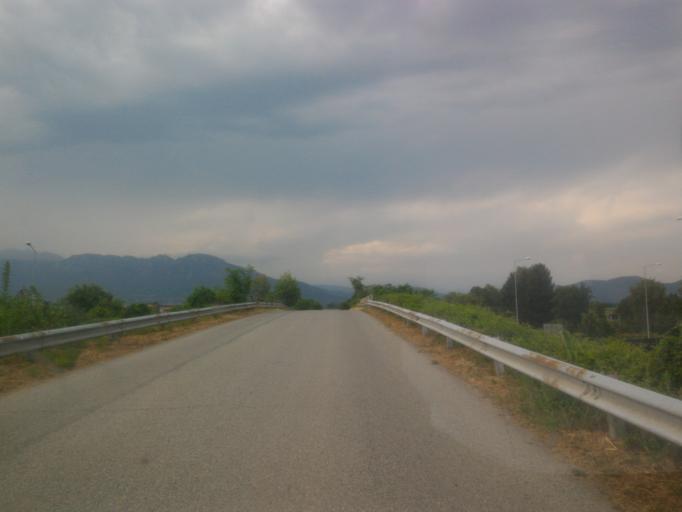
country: IT
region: Piedmont
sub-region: Provincia di Torino
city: Riva
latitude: 44.8918
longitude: 7.3955
